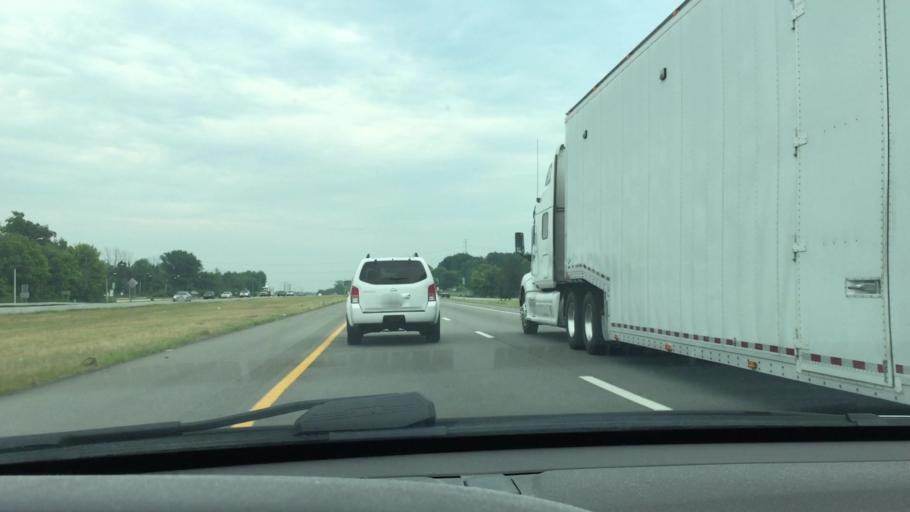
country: US
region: Ohio
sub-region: Warren County
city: Morrow
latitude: 39.4146
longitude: -84.1262
